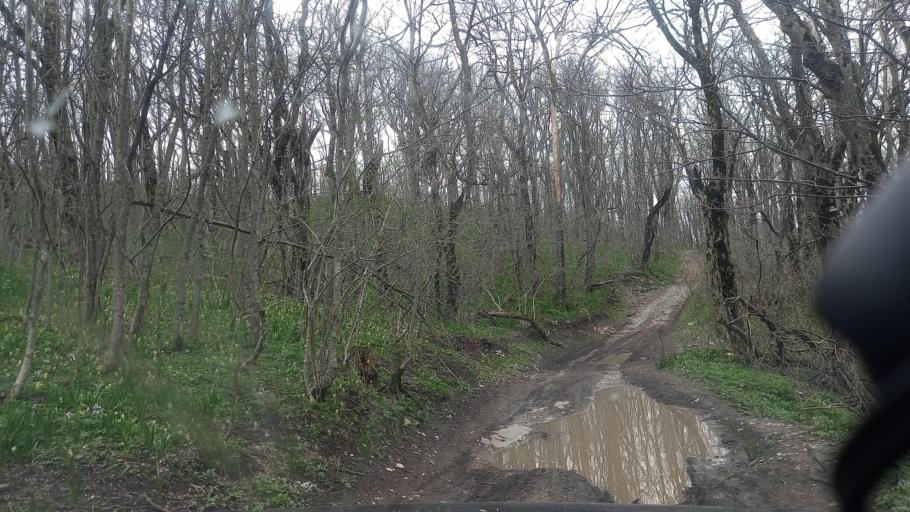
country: RU
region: Krasnodarskiy
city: Gelendzhik
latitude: 44.6136
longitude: 38.2079
